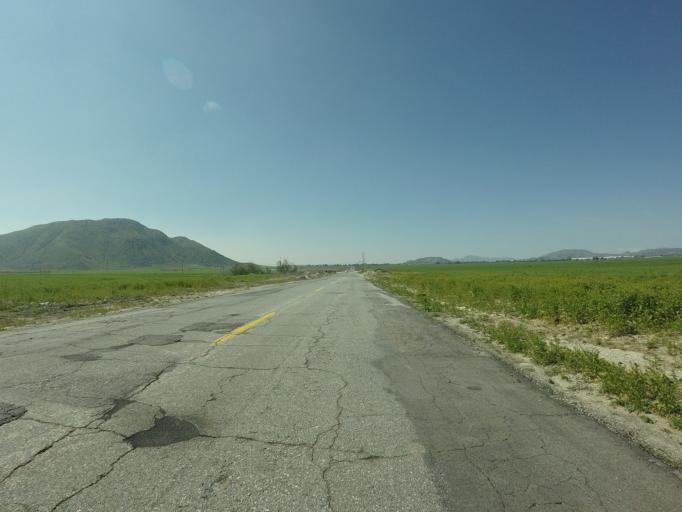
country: US
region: California
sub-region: Riverside County
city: Lakeview
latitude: 33.9195
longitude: -117.1183
